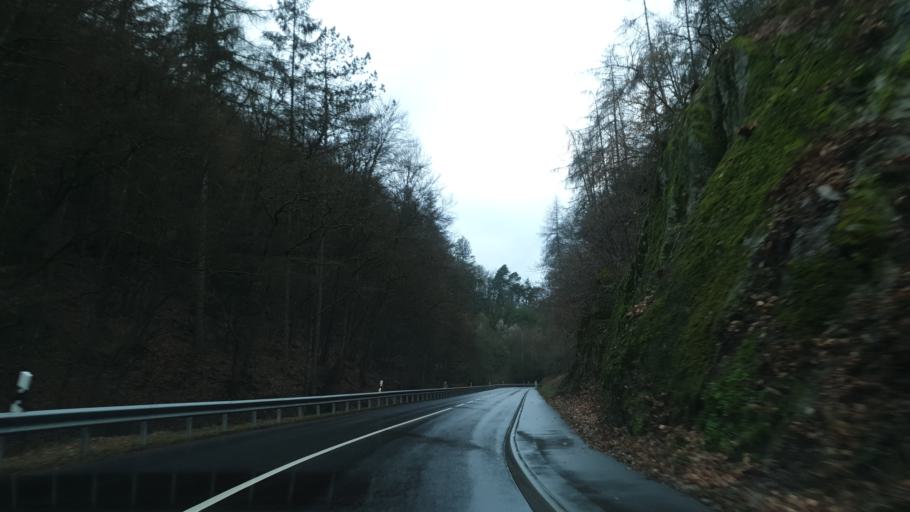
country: DE
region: Rheinland-Pfalz
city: Laurenburg
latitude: 50.3371
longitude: 7.9041
